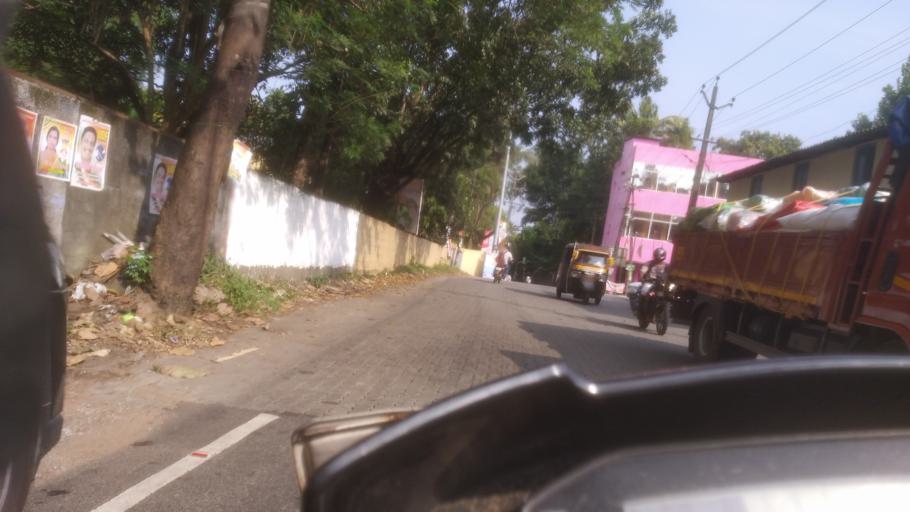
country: IN
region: Kerala
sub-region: Ernakulam
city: Angamali
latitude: 10.1655
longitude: 76.4110
